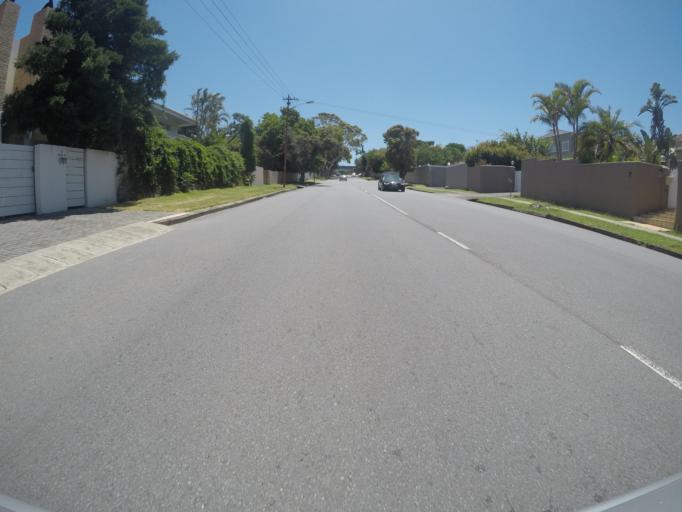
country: ZA
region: Eastern Cape
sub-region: Buffalo City Metropolitan Municipality
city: East London
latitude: -32.9876
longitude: 27.8963
